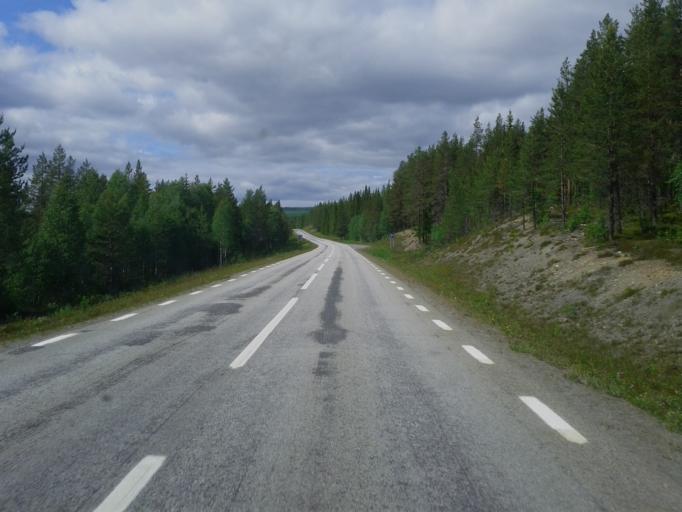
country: SE
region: Vaesterbotten
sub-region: Storumans Kommun
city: Fristad
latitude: 65.3844
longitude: 16.4864
